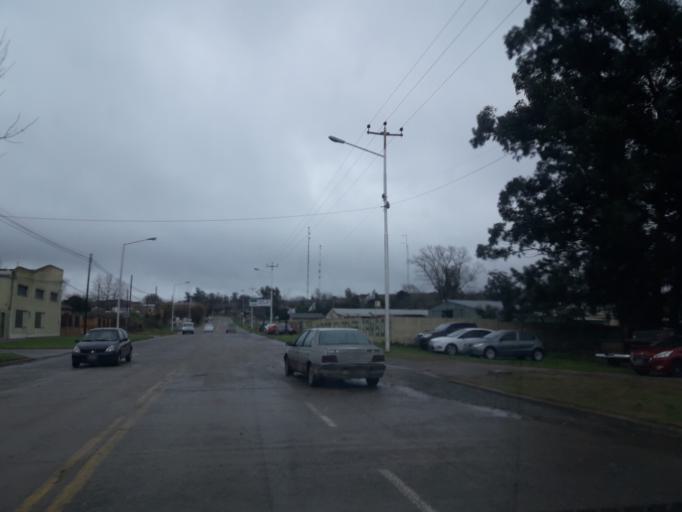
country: AR
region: Buenos Aires
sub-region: Partido de Tandil
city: Tandil
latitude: -37.3222
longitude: -59.1667
